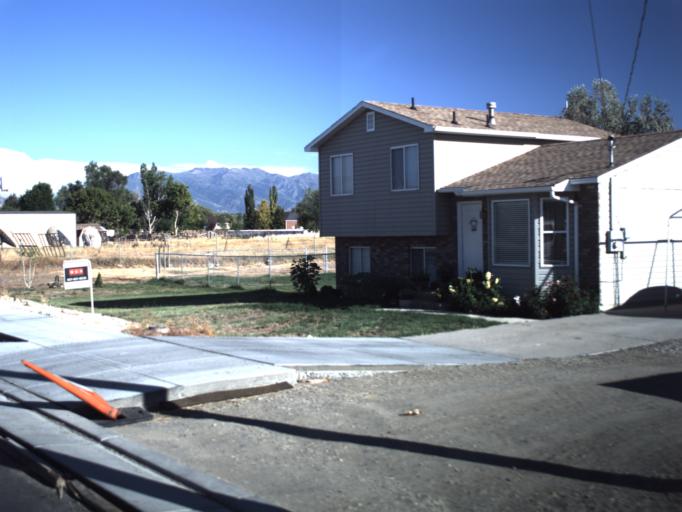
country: US
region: Utah
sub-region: Weber County
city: West Haven
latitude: 41.1907
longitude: -112.0825
